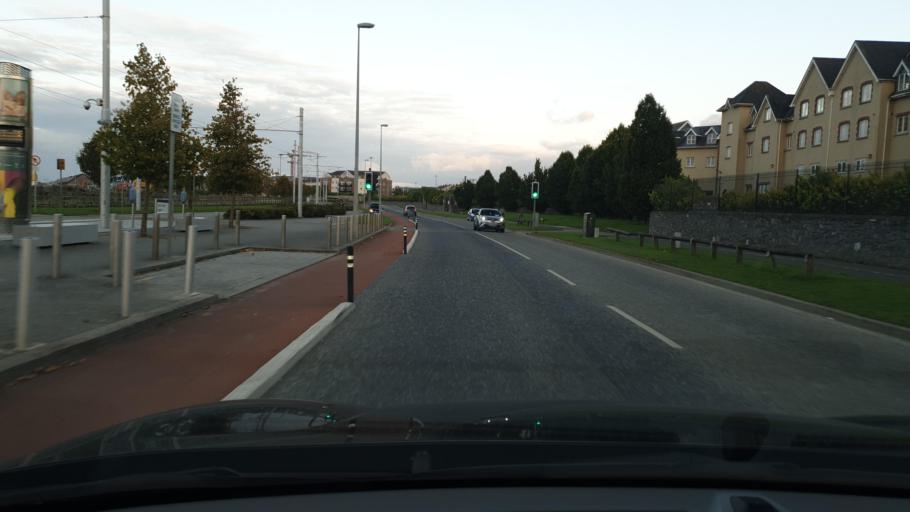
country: IE
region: Leinster
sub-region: South Dublin
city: Saggart
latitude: 53.2846
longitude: -6.4381
